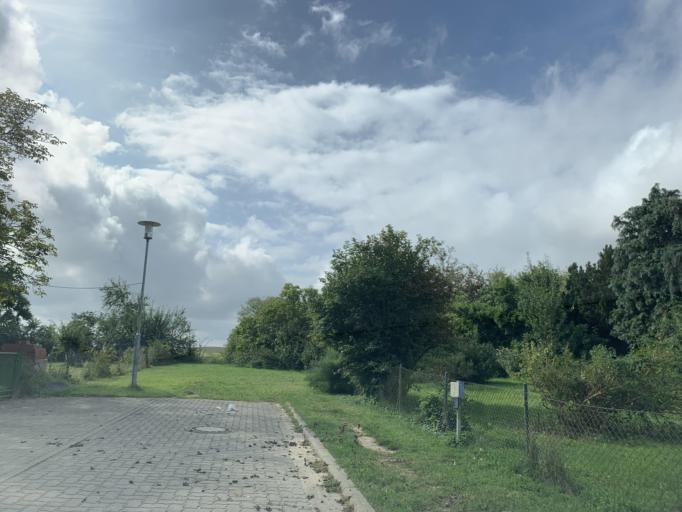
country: DE
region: Mecklenburg-Vorpommern
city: Blankensee
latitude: 53.3901
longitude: 13.3147
